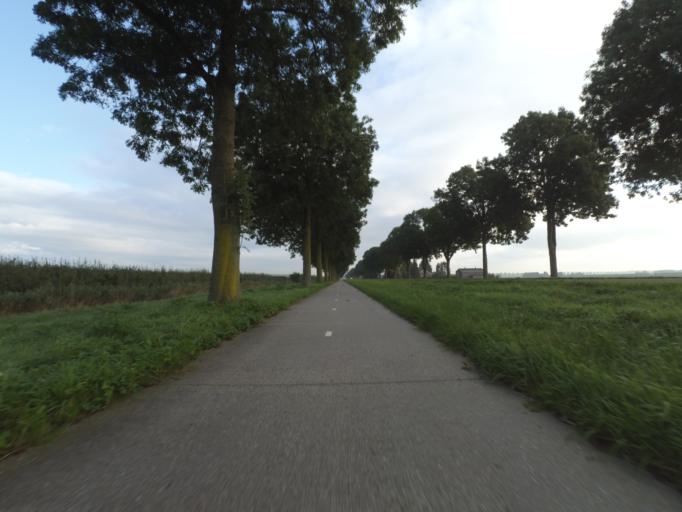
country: NL
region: Flevoland
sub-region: Gemeente Dronten
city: Dronten
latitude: 52.5040
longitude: 5.6815
